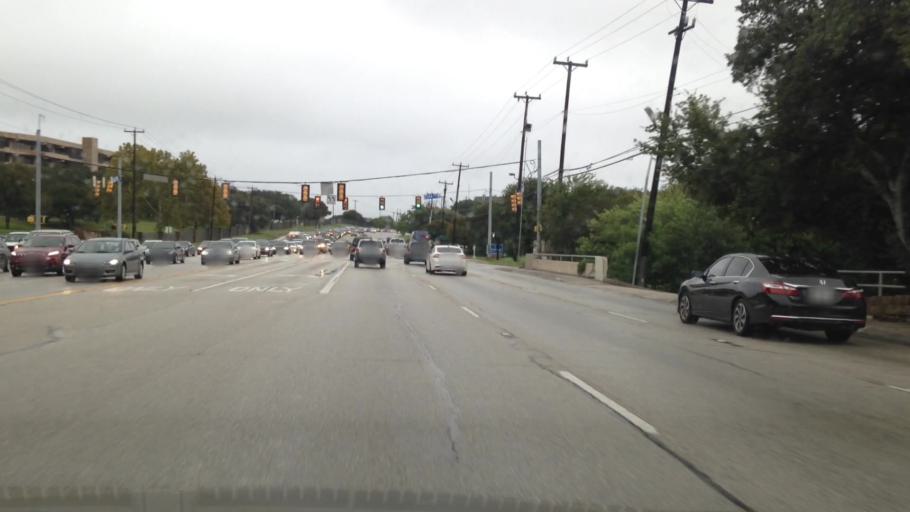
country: US
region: Texas
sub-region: Bexar County
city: Shavano Park
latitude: 29.5382
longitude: -98.5787
